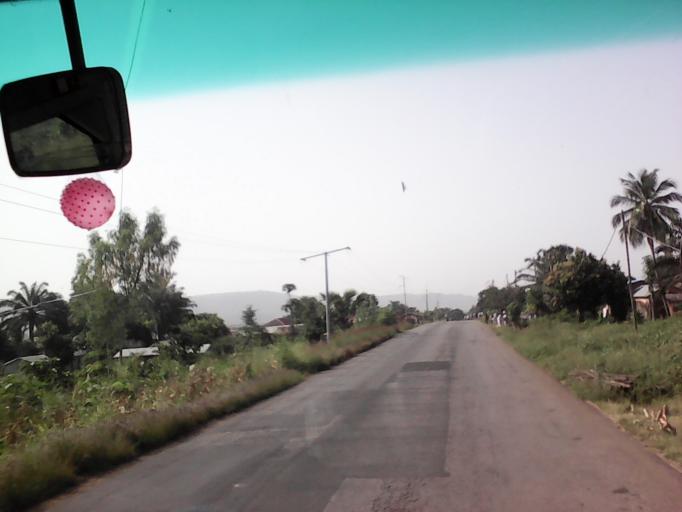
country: TG
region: Centrale
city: Sokode
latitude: 9.1111
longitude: 1.1445
